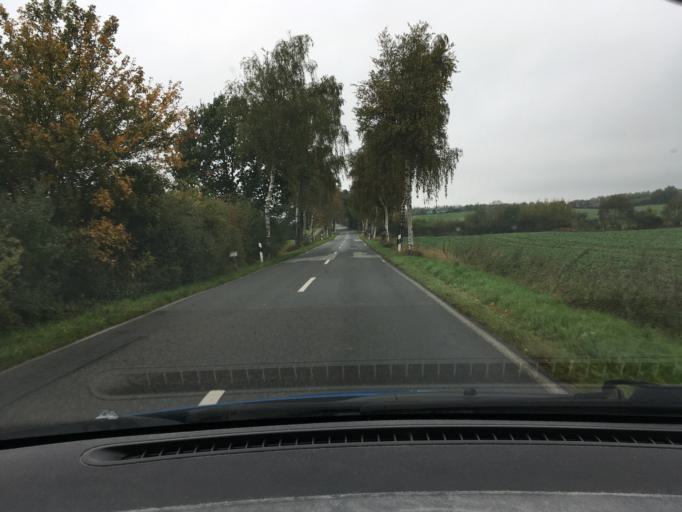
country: DE
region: Schleswig-Holstein
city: Bosau
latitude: 54.0935
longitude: 10.4680
